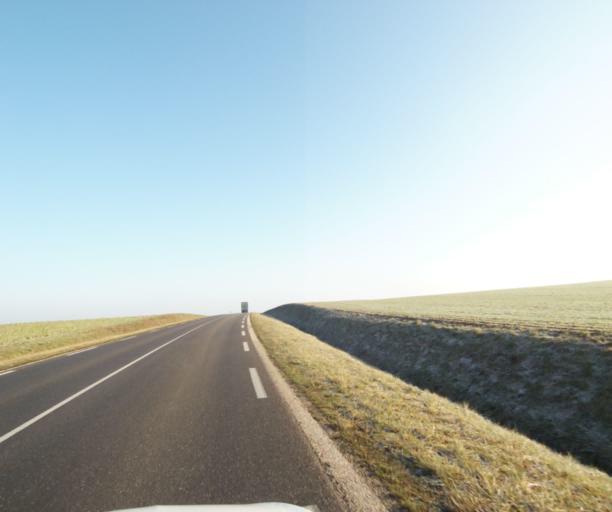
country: FR
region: Champagne-Ardenne
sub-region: Departement de la Haute-Marne
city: Montier-en-Der
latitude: 48.4528
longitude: 4.7419
